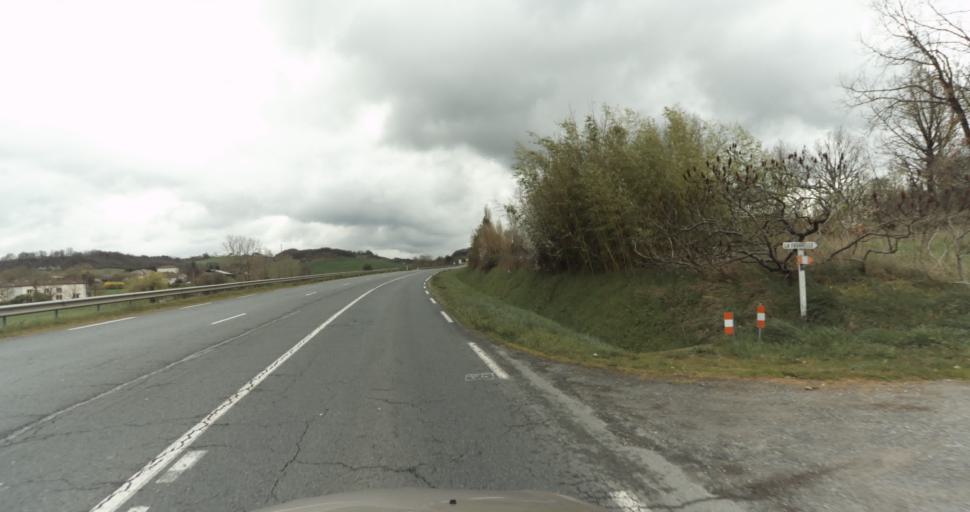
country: FR
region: Midi-Pyrenees
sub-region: Departement du Tarn
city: Puygouzon
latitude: 43.8778
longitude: 2.1764
